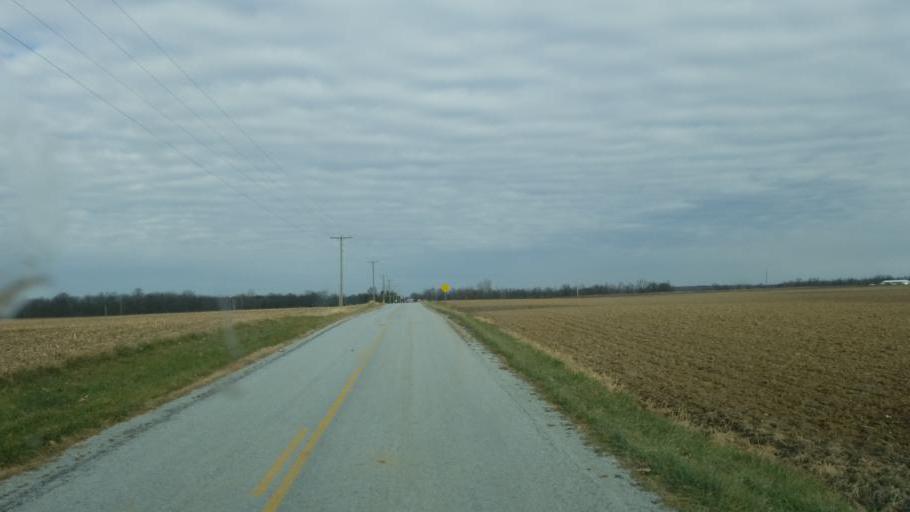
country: US
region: Ohio
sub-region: Hardin County
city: Forest
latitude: 40.6410
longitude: -83.4199
